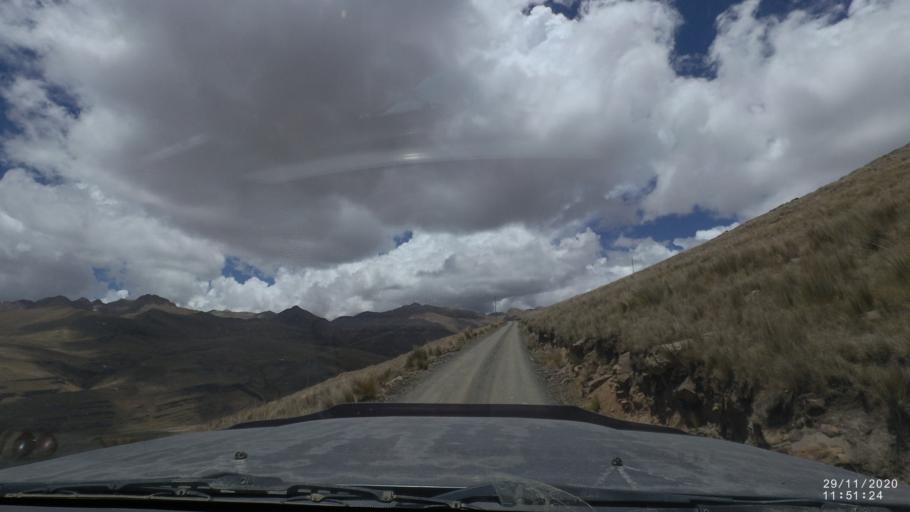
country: BO
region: Cochabamba
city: Cochabamba
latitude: -17.1720
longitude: -66.2610
